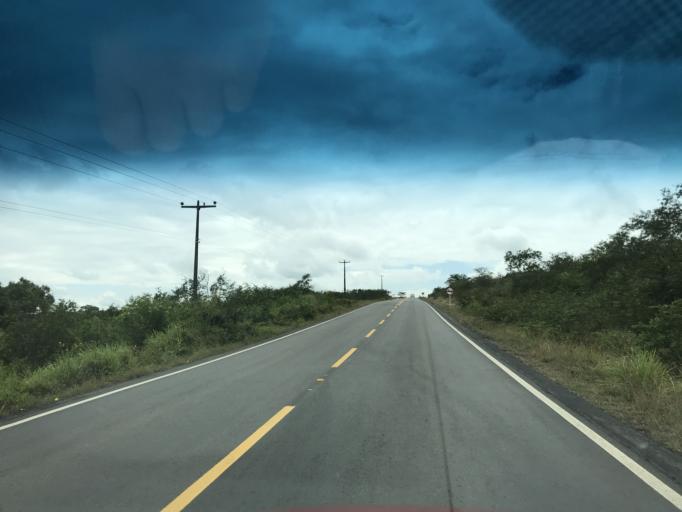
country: BR
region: Bahia
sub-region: Conceicao Do Almeida
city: Conceicao do Almeida
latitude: -12.6687
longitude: -39.2868
